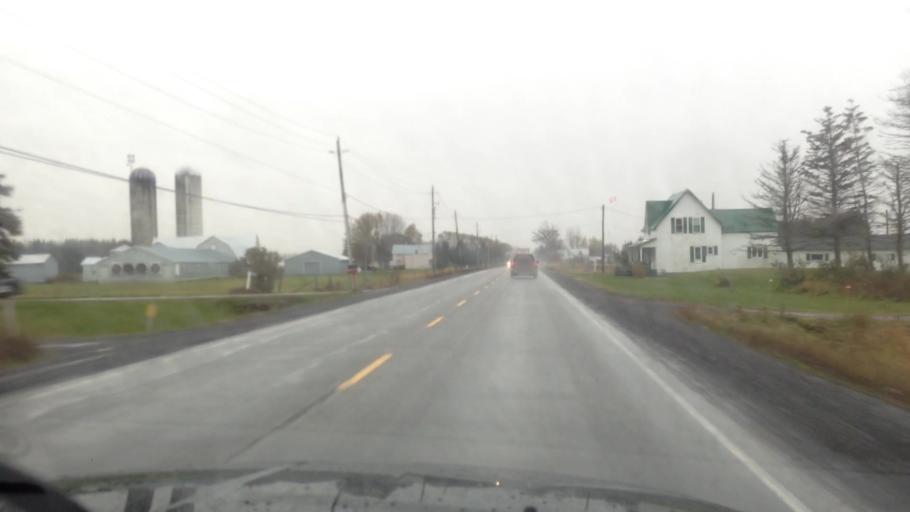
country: CA
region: Ontario
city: Bourget
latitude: 45.3128
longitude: -75.3356
